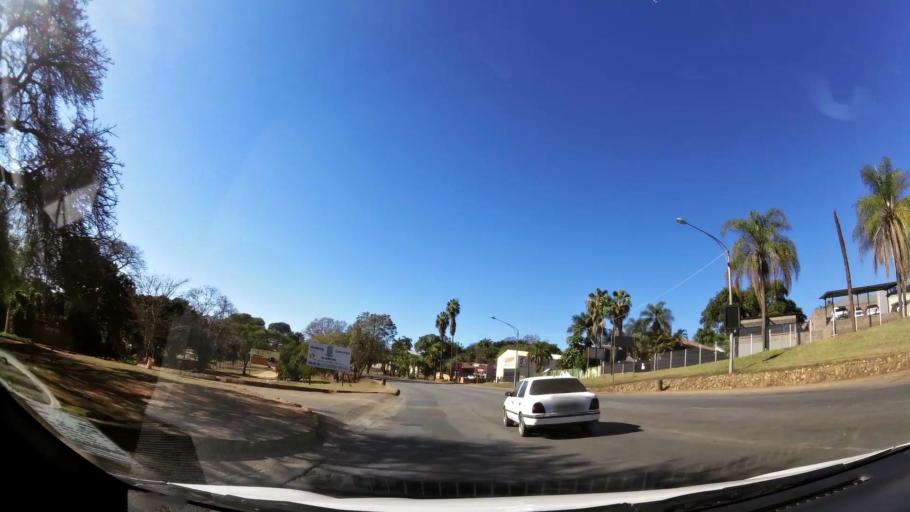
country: ZA
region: Limpopo
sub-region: Mopani District Municipality
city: Tzaneen
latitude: -23.8325
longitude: 30.1654
